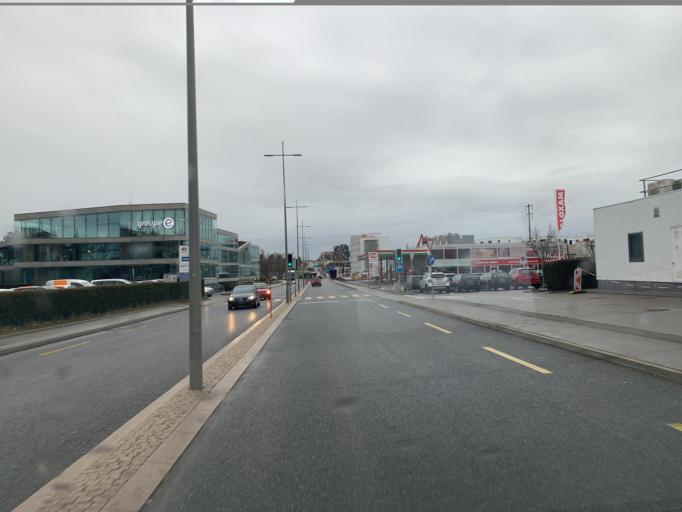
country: CH
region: Fribourg
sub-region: Sarine District
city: Fribourg
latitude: 46.8218
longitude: 7.1516
